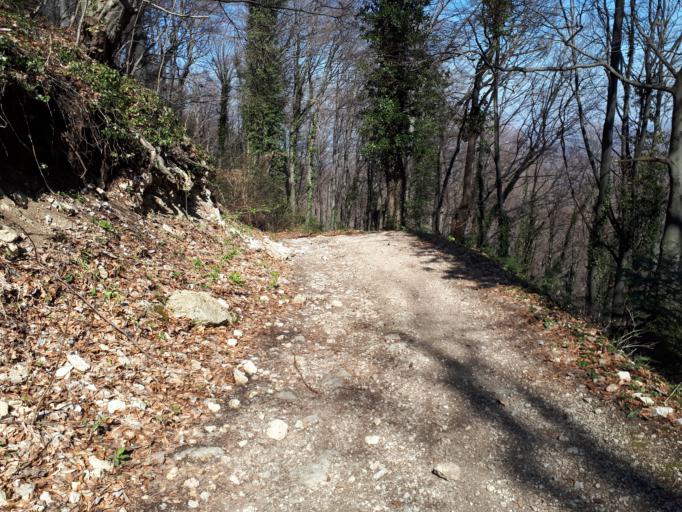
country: HR
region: Varazdinska
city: Ivanec
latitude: 46.1821
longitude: 16.1484
